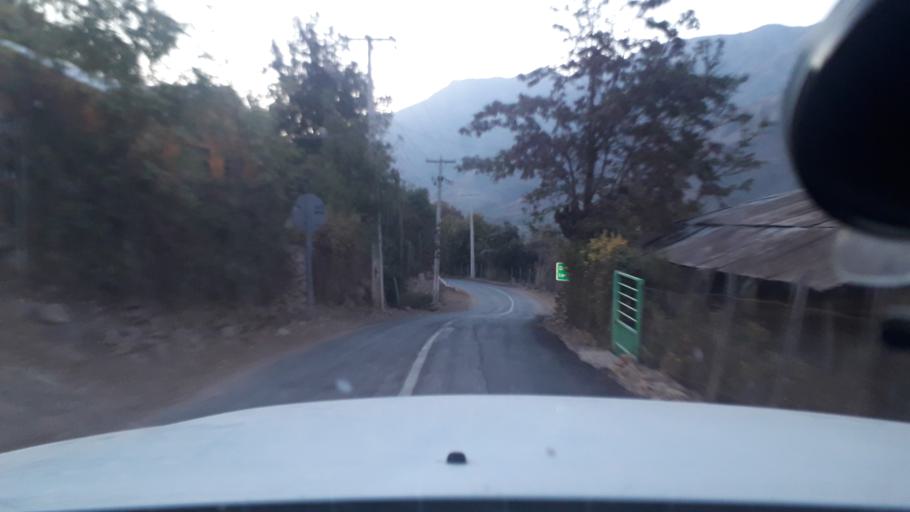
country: CL
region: Valparaiso
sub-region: Provincia de Marga Marga
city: Limache
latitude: -33.1796
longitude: -71.1154
